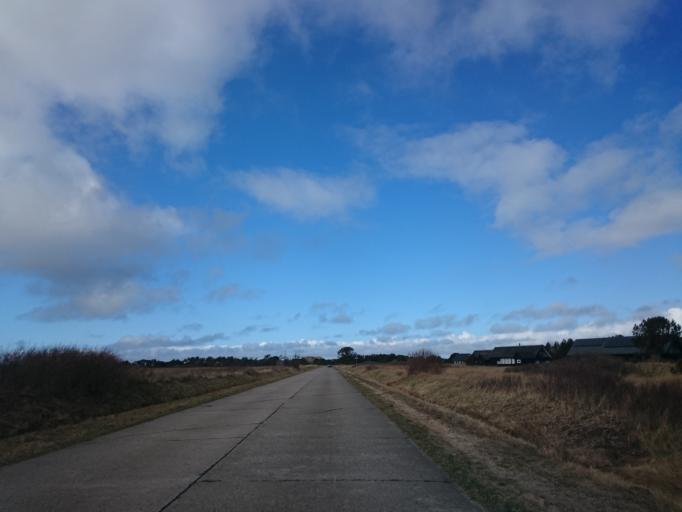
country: DK
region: North Denmark
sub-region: Frederikshavn Kommune
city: Skagen
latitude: 57.6597
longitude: 10.4026
